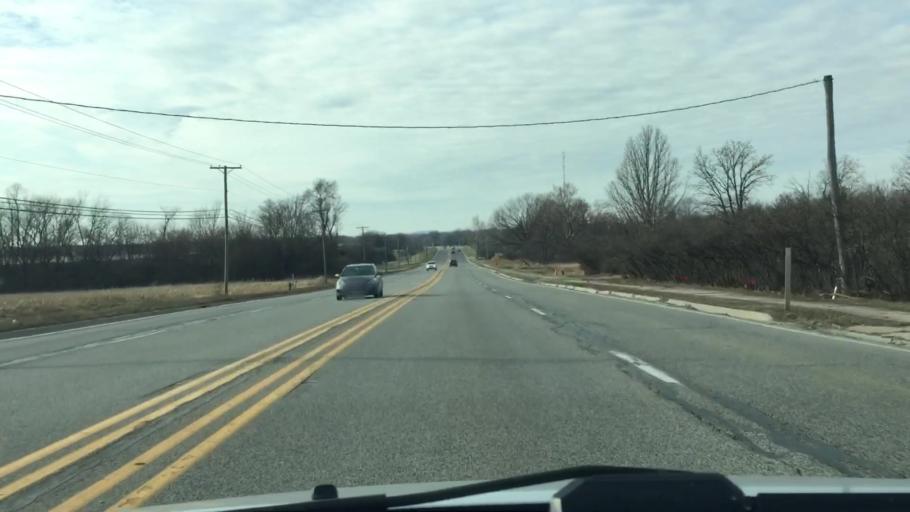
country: US
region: Illinois
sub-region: Kane County
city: Geneva
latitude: 41.8689
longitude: -88.2831
